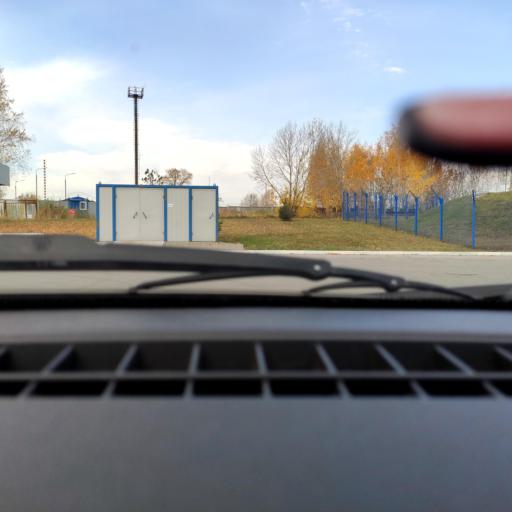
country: RU
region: Bashkortostan
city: Ufa
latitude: 54.8293
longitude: 56.1254
